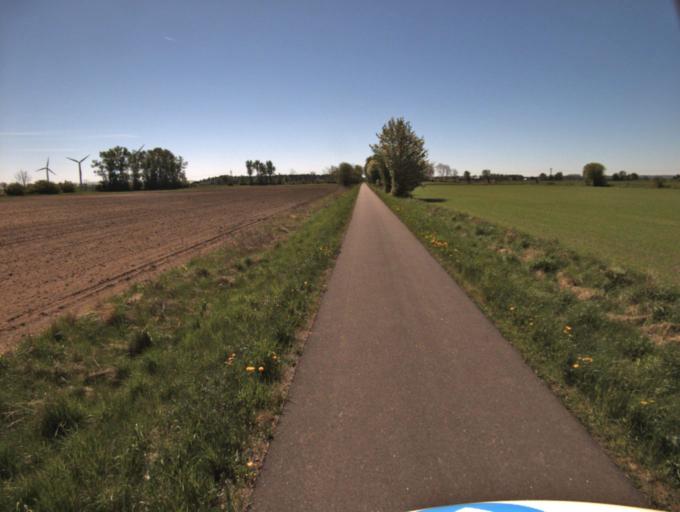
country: SE
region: Skane
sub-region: Kristianstads Kommun
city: Norra Asum
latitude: 55.9650
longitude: 14.1579
